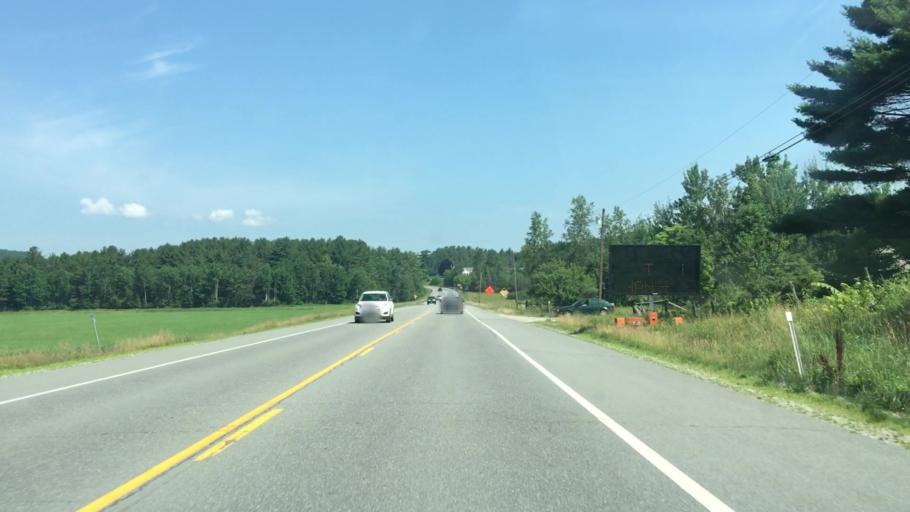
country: US
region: New Hampshire
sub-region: Sullivan County
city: Sunapee
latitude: 43.3646
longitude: -72.1207
